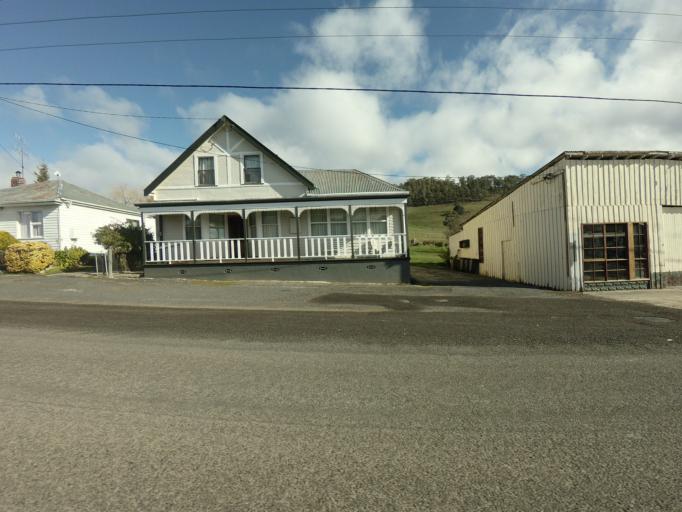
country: AU
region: Tasmania
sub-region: Derwent Valley
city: New Norfolk
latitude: -42.6140
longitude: 146.7141
